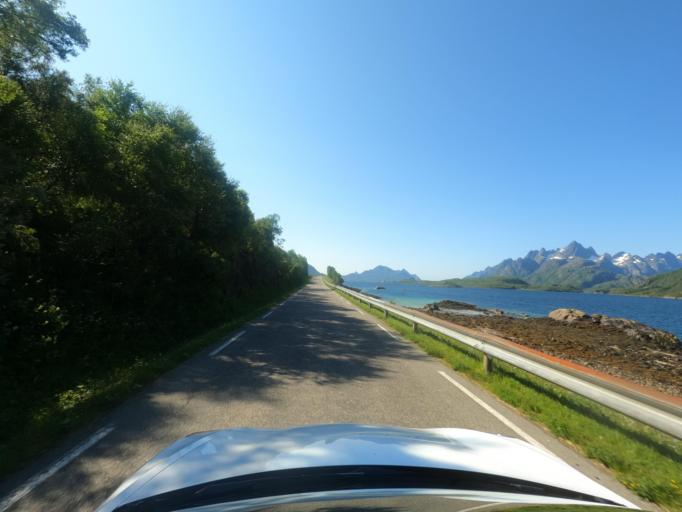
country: NO
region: Nordland
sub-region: Hadsel
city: Stokmarknes
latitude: 68.3755
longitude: 15.0791
